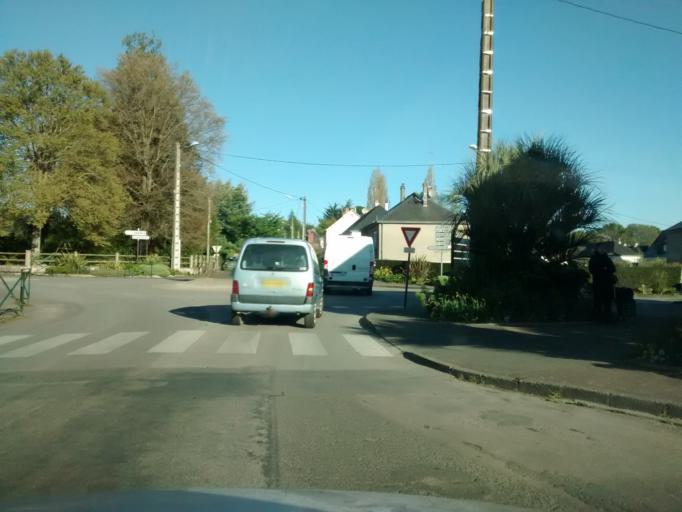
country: FR
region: Brittany
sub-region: Departement du Morbihan
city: Malestroit
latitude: 47.8099
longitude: -2.3867
